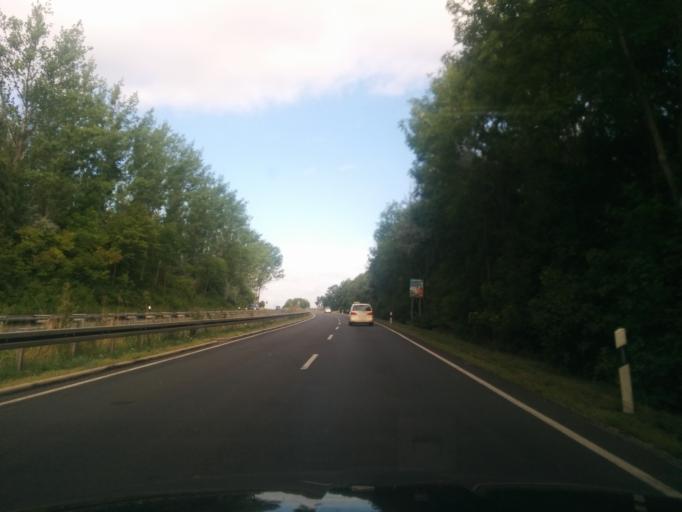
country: DE
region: Saxony-Anhalt
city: Zscherben
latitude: 51.4813
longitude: 11.8802
